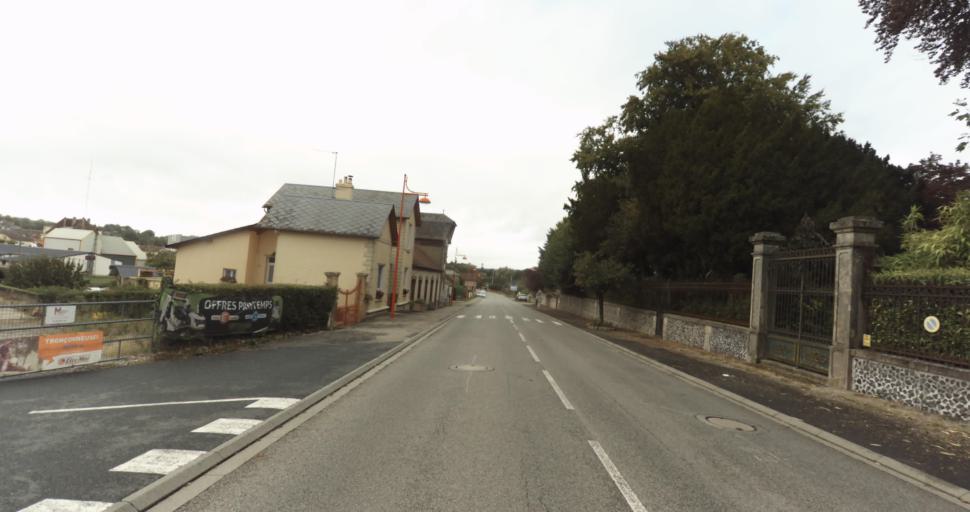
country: FR
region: Lower Normandy
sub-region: Departement de l'Orne
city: Sainte-Gauburge-Sainte-Colombe
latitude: 48.7157
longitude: 0.4329
